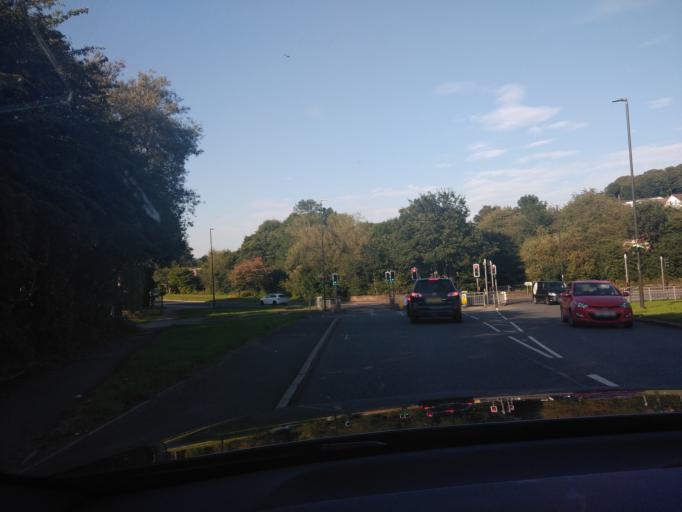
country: GB
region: England
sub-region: Derbyshire
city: Dronfield
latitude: 53.3085
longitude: -1.4782
